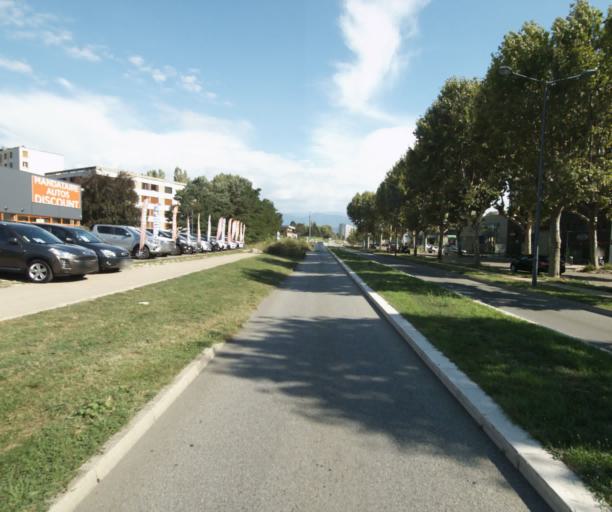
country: FR
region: Rhone-Alpes
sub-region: Departement de l'Isere
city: Fontaine
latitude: 45.1876
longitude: 5.6859
